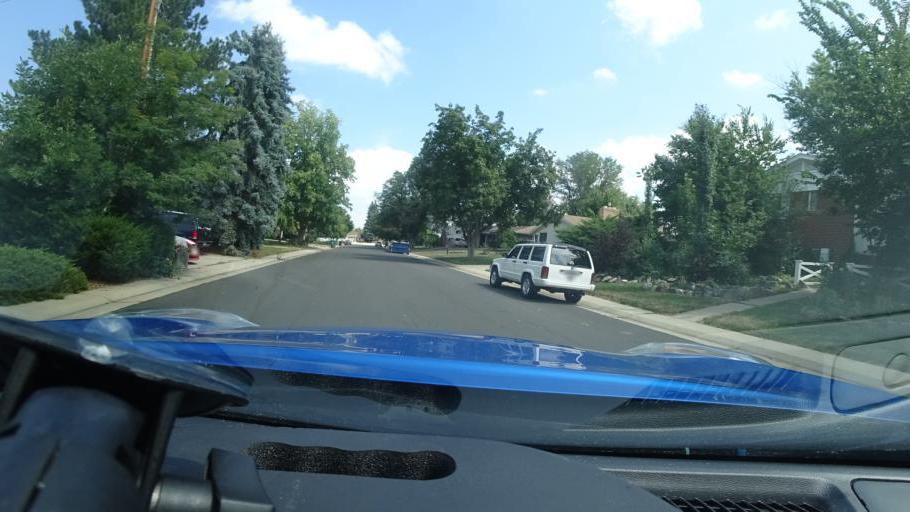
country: US
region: Colorado
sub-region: Adams County
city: Aurora
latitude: 39.7238
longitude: -104.8551
